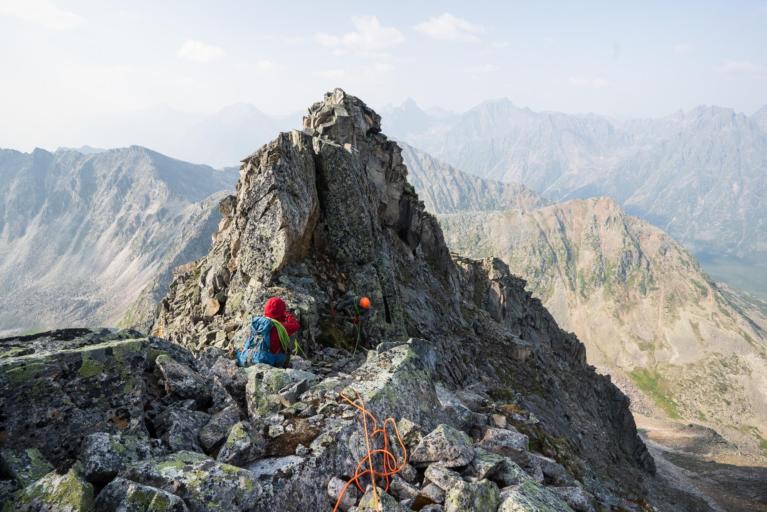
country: RU
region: Transbaikal Territory
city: Kuanda
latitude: 56.7899
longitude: 116.8197
